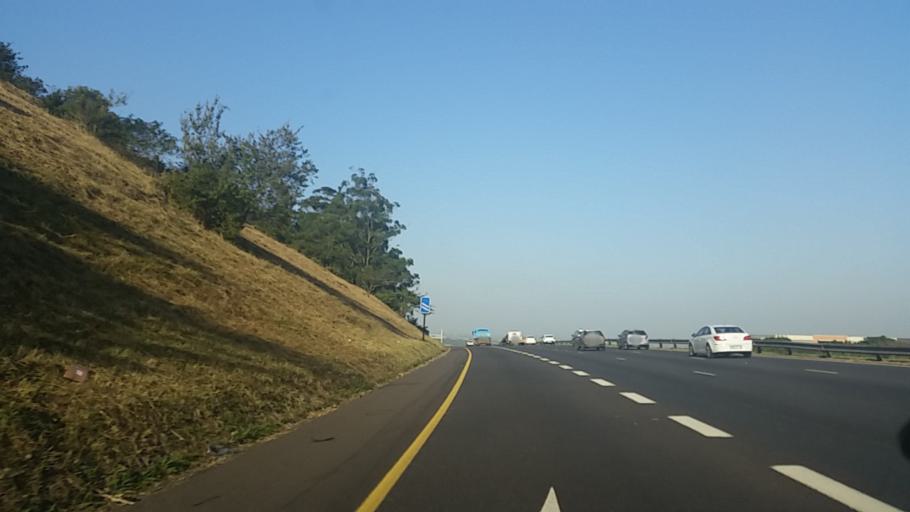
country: ZA
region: KwaZulu-Natal
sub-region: eThekwini Metropolitan Municipality
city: Berea
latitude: -29.8451
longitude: 30.9232
